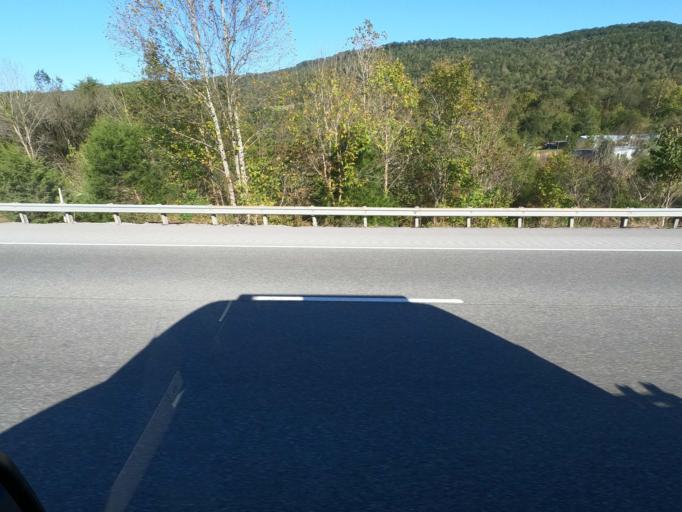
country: US
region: Tennessee
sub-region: Marion County
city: Monteagle
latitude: 35.1733
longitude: -85.7939
